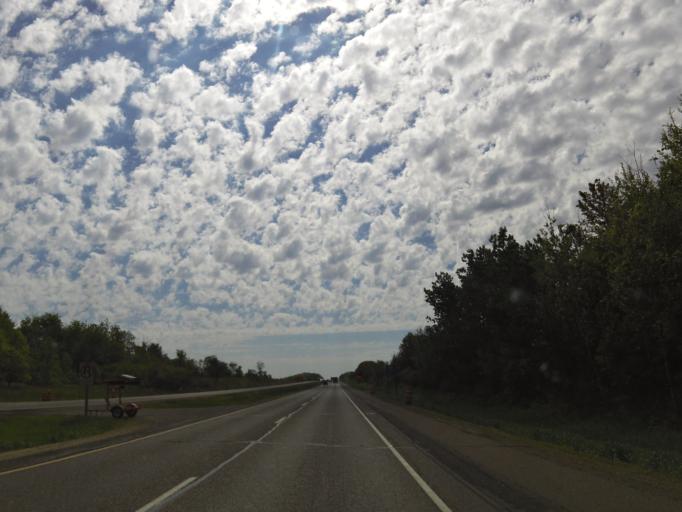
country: US
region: Wisconsin
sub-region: Dunn County
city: Colfax
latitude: 44.8908
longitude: -91.7406
